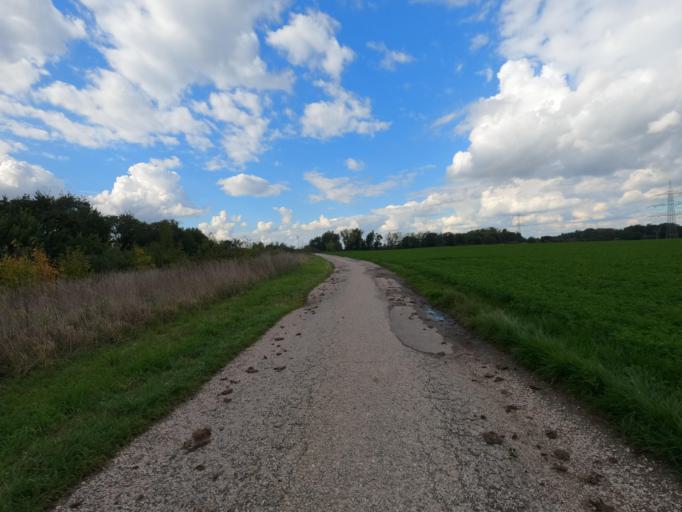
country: DE
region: North Rhine-Westphalia
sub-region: Regierungsbezirk Koln
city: Aldenhoven
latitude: 50.9274
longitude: 6.3080
